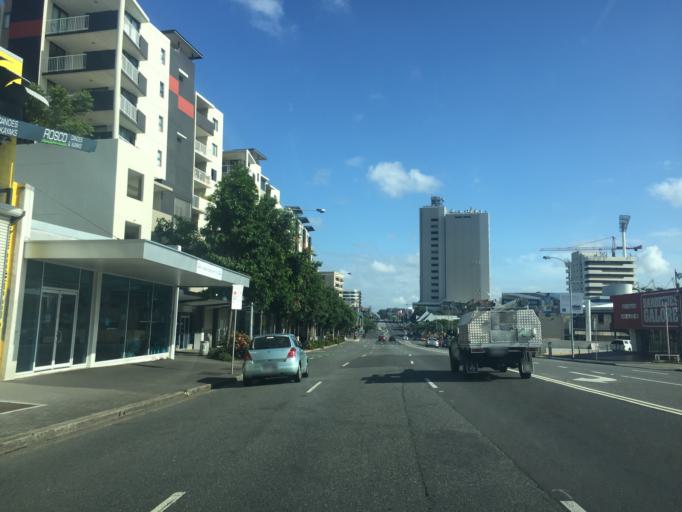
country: AU
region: Queensland
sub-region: Brisbane
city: Woolloongabba
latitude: -27.4881
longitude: 153.0359
